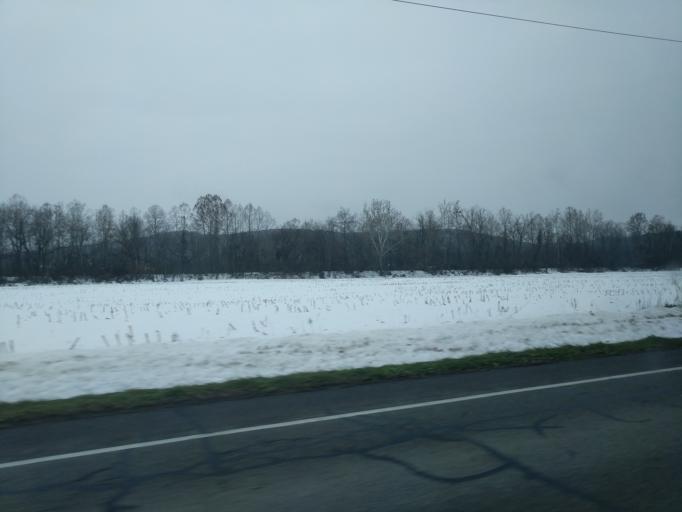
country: US
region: Pennsylvania
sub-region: Tioga County
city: Mansfield
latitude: 41.9144
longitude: -77.1331
